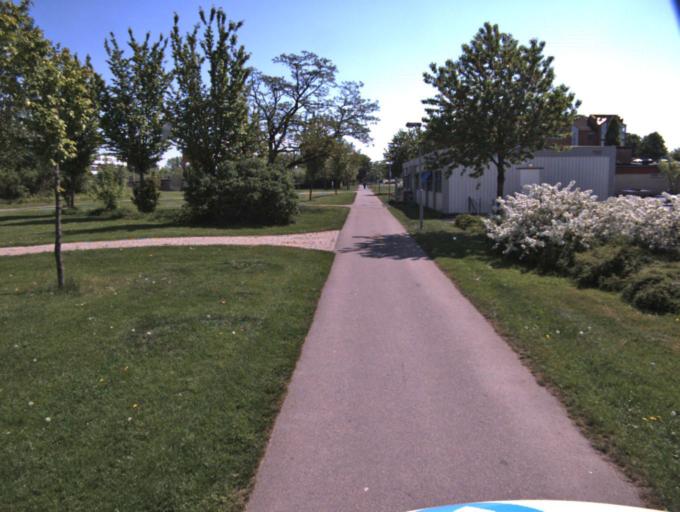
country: SE
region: Skane
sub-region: Kristianstads Kommun
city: Kristianstad
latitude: 56.0581
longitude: 14.1579
